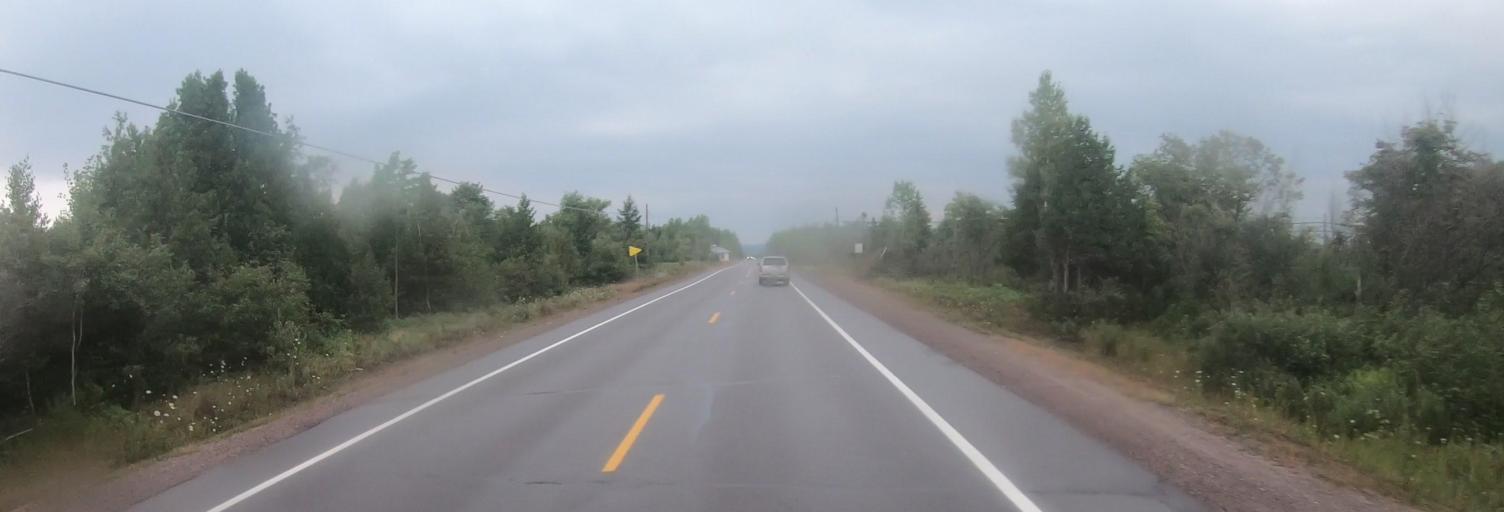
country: US
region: Michigan
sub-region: Houghton County
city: Laurium
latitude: 47.2768
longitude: -88.4149
